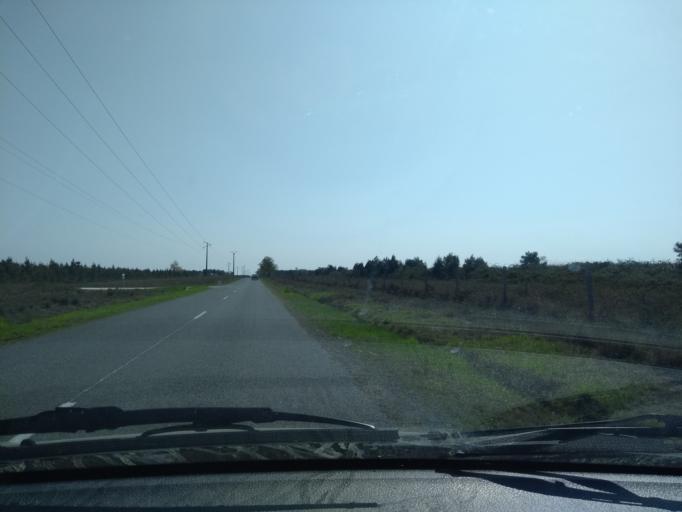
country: FR
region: Aquitaine
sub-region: Departement de la Gironde
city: Belin-Beliet
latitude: 44.5277
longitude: -0.7084
